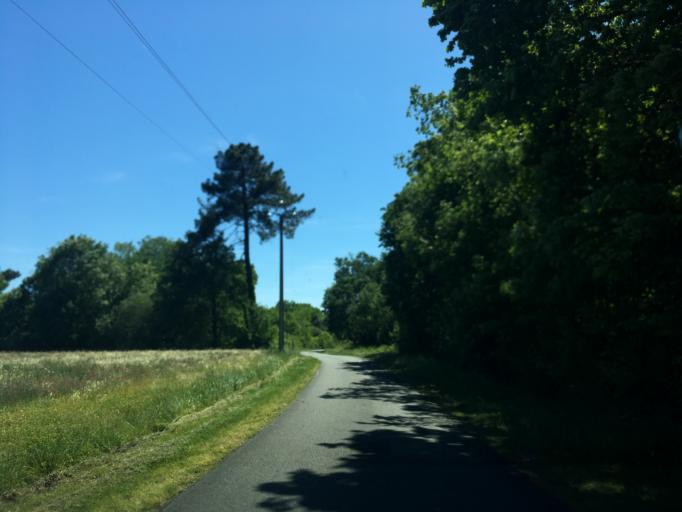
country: FR
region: Aquitaine
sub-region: Departement de la Gironde
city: Lesparre-Medoc
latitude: 45.3034
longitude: -0.8868
